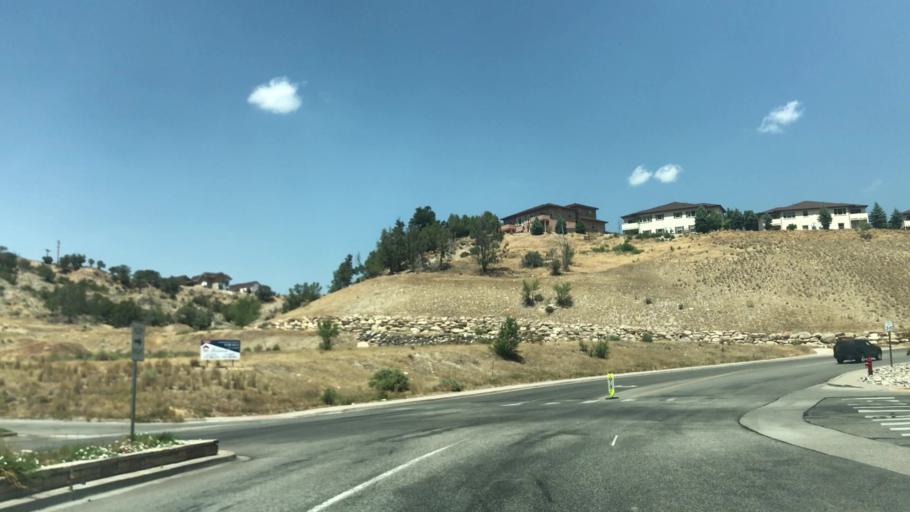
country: US
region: Colorado
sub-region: Garfield County
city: New Castle
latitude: 39.5685
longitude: -107.5160
